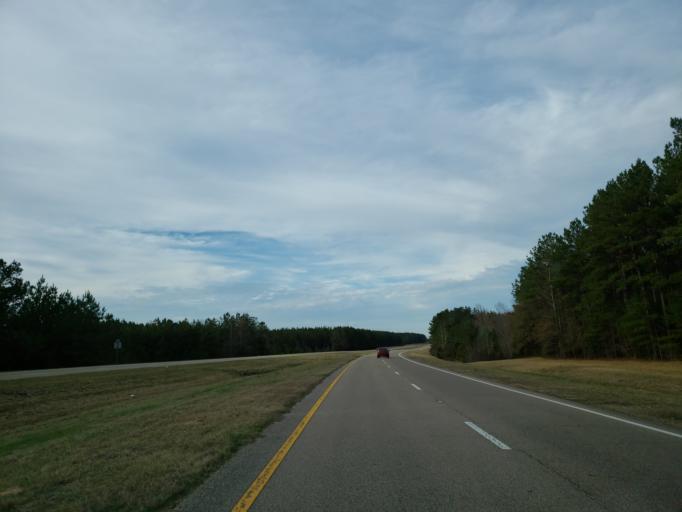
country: US
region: Mississippi
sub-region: Wayne County
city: Waynesboro
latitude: 31.6342
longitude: -88.5931
